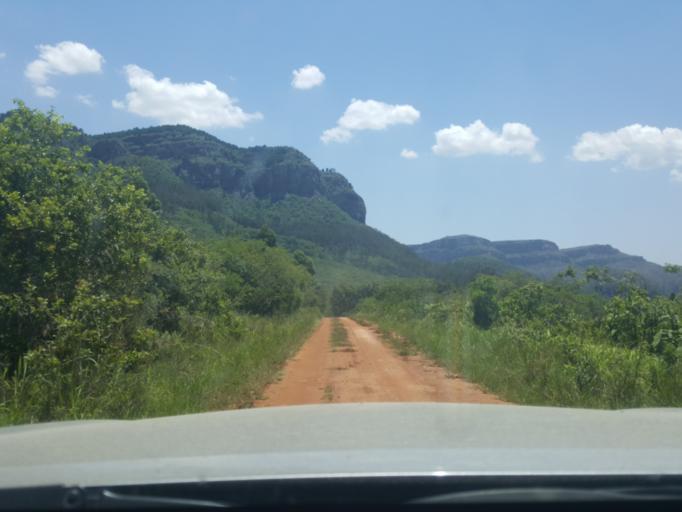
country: ZA
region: Limpopo
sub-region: Mopani District Municipality
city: Hoedspruit
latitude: -24.5950
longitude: 30.8573
